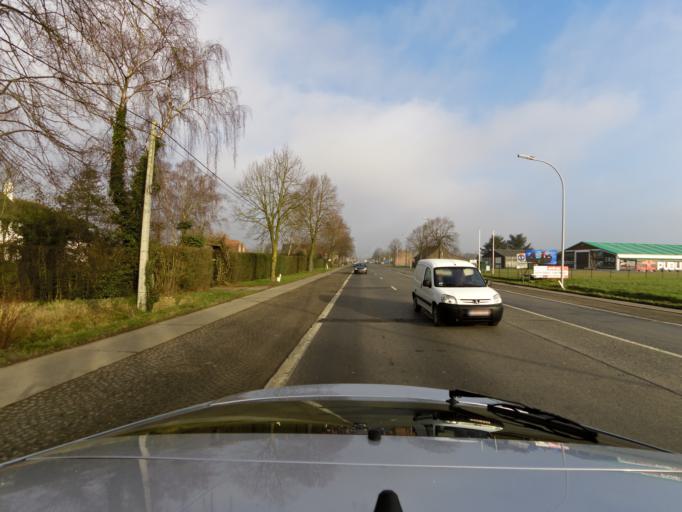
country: BE
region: Flanders
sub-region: Provincie West-Vlaanderen
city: Torhout
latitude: 51.0472
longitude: 3.1057
